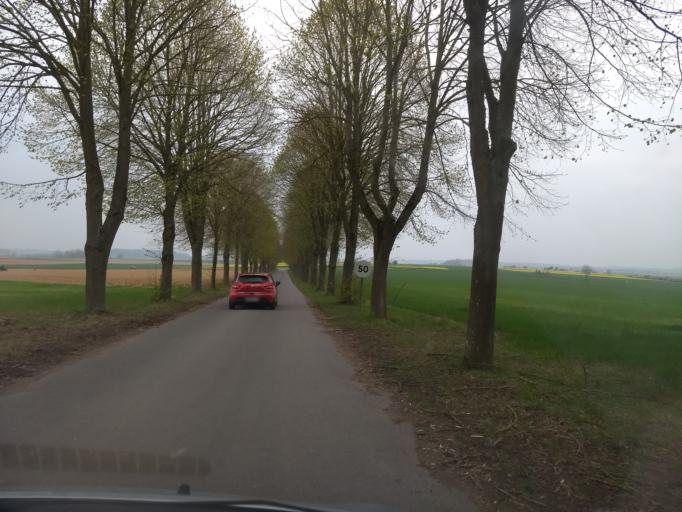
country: FR
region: Nord-Pas-de-Calais
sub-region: Departement du Pas-de-Calais
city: Maroeuil
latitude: 50.3358
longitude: 2.7020
